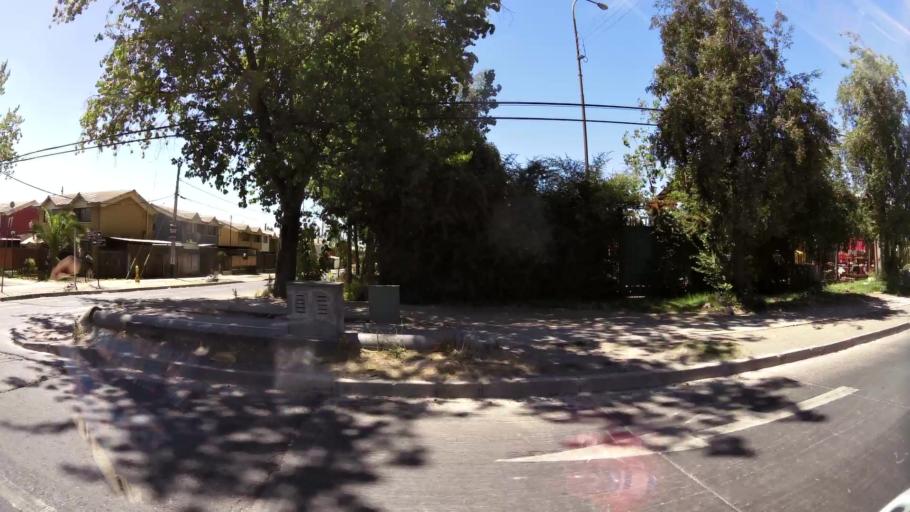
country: CL
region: O'Higgins
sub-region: Provincia de Cachapoal
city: Rancagua
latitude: -34.1599
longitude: -70.7597
